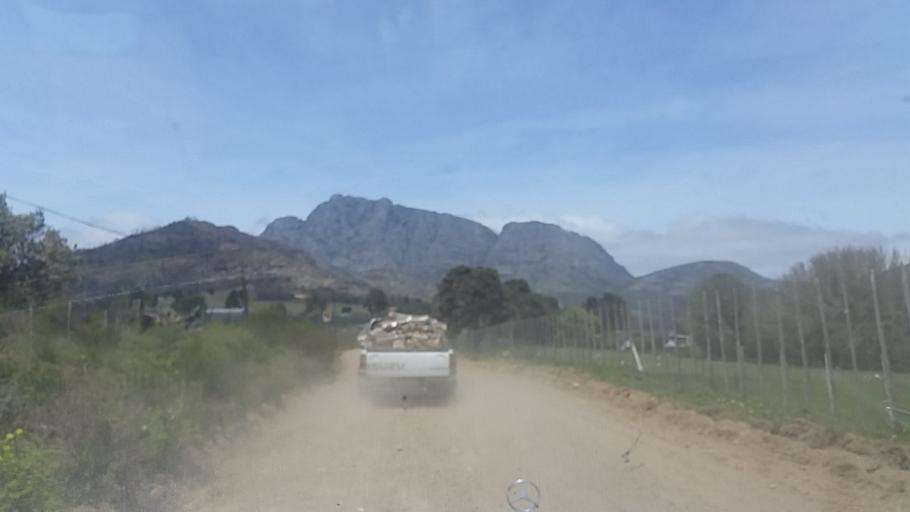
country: ZA
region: Western Cape
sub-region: Eden District Municipality
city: George
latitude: -33.8558
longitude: 22.4486
